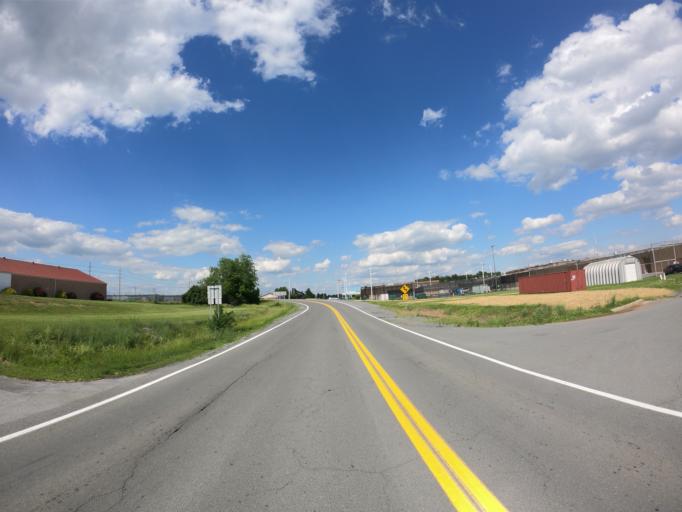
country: US
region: West Virginia
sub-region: Berkeley County
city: Martinsburg
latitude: 39.4352
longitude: -77.9581
